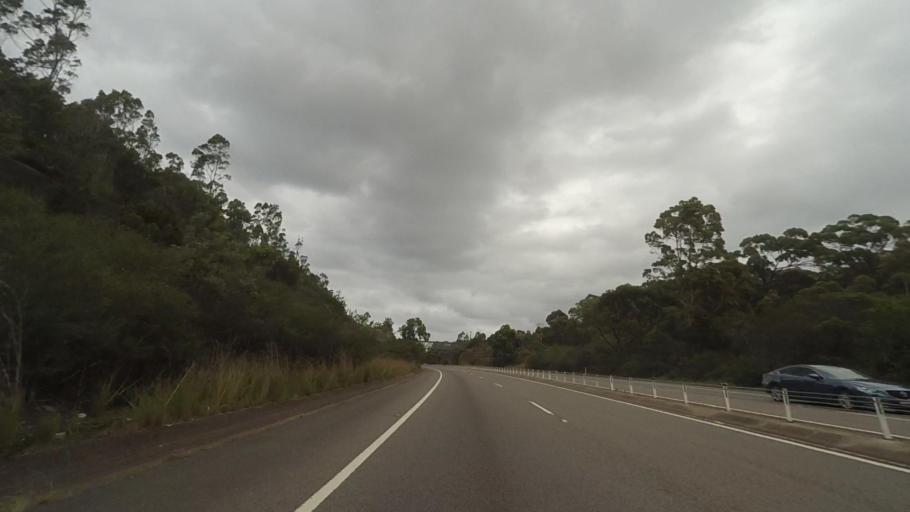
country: AU
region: New South Wales
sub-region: Lake Macquarie Shire
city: Arcadia vale
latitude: -33.1182
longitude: 151.6290
